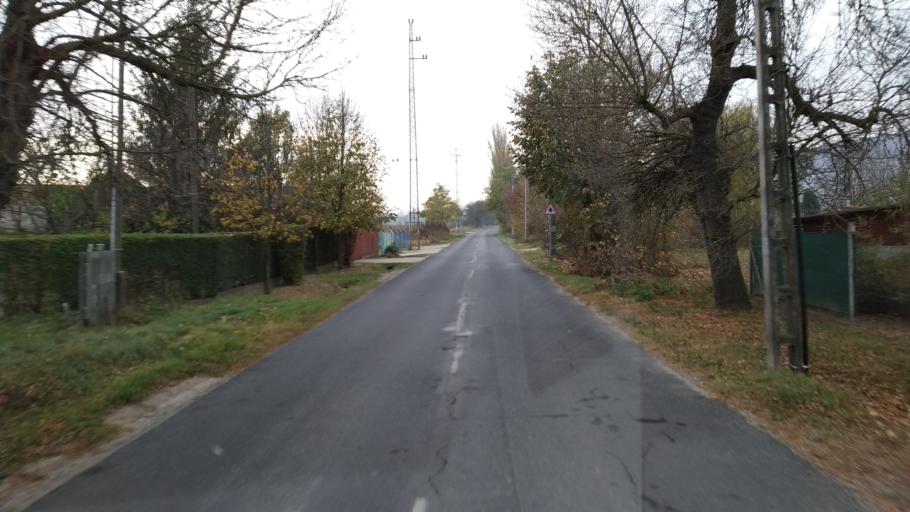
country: HU
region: Pest
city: Tahitotfalu
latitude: 47.7683
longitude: 19.0874
